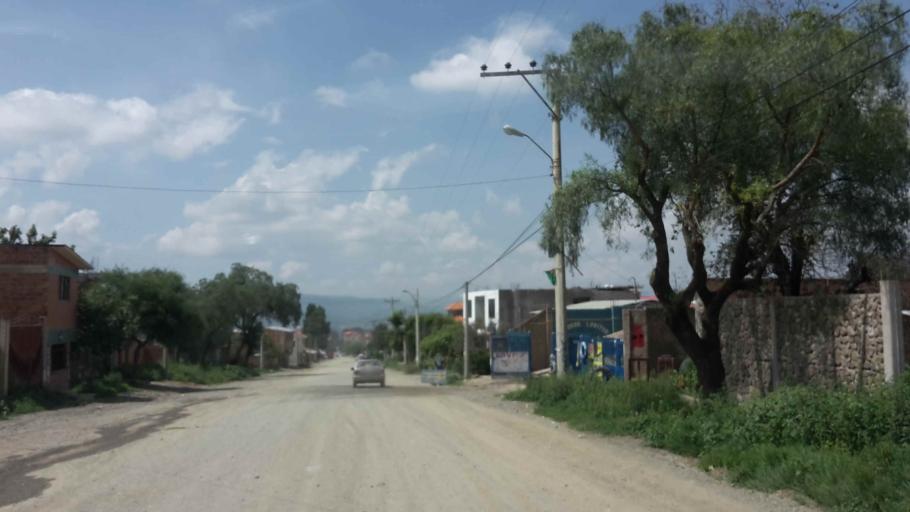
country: BO
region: Cochabamba
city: Cochabamba
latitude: -17.3282
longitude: -66.2180
